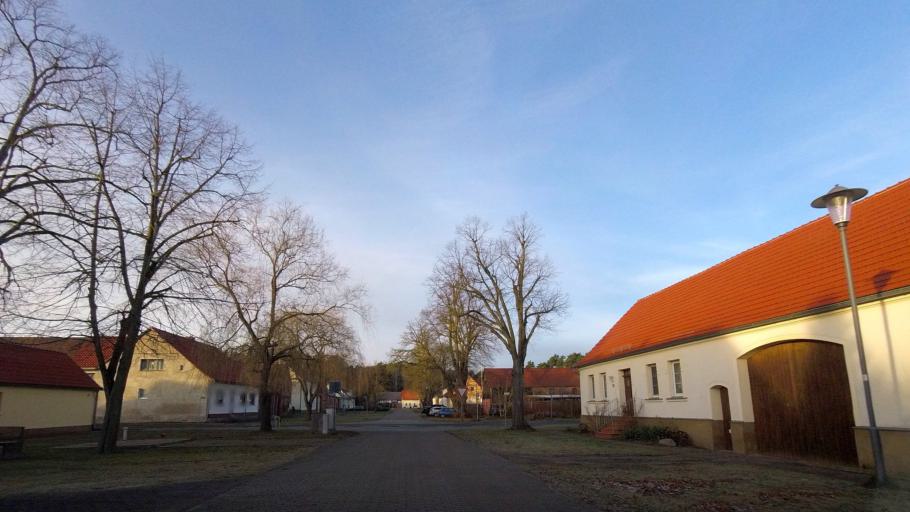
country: DE
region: Brandenburg
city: Niedergorsdorf
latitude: 52.0489
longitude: 12.9434
